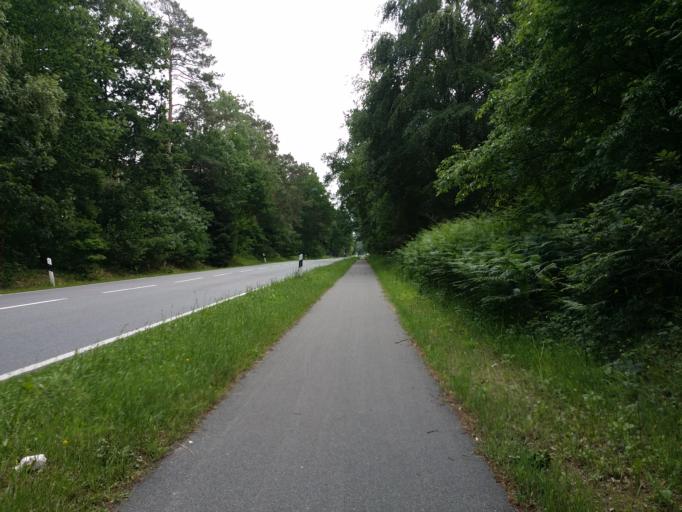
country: DE
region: Lower Saxony
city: Zetel
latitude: 53.3995
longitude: 7.9187
